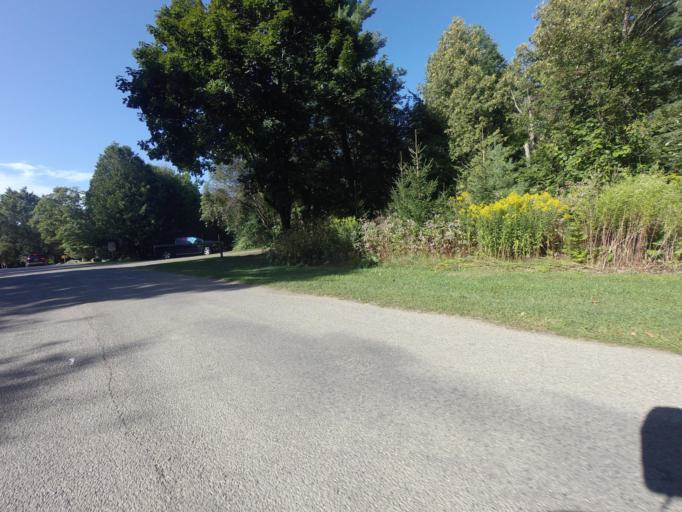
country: CA
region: Ontario
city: Waterloo
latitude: 43.6693
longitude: -80.4501
